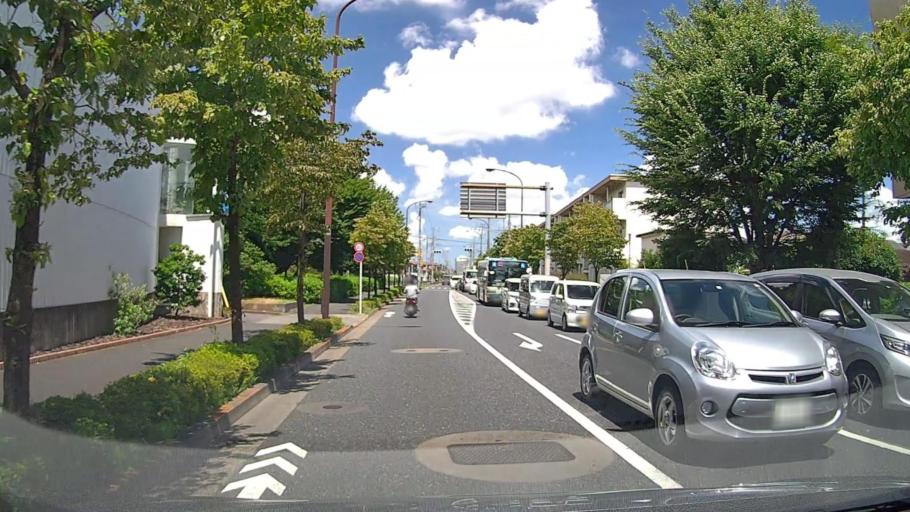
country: JP
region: Tokyo
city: Nishi-Tokyo-shi
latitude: 35.7319
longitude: 139.5432
